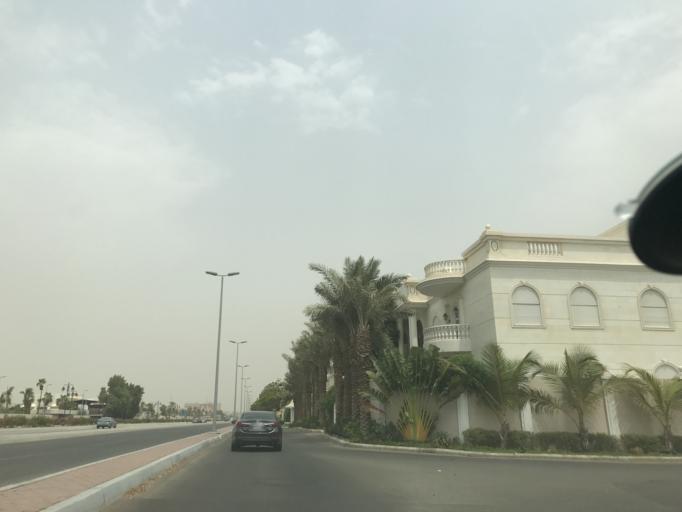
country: SA
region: Makkah
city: Jeddah
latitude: 21.5539
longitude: 39.1586
